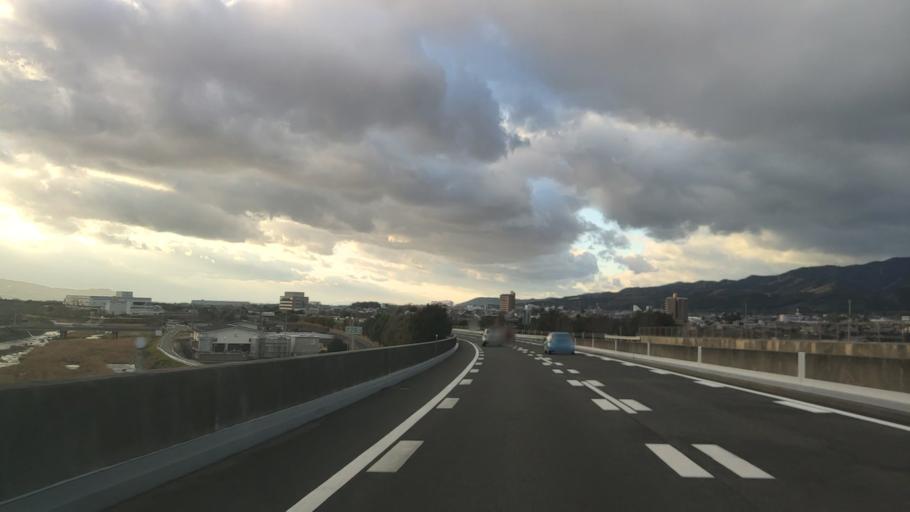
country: JP
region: Ehime
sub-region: Shikoku-chuo Shi
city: Matsuyama
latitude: 33.7939
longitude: 132.9106
